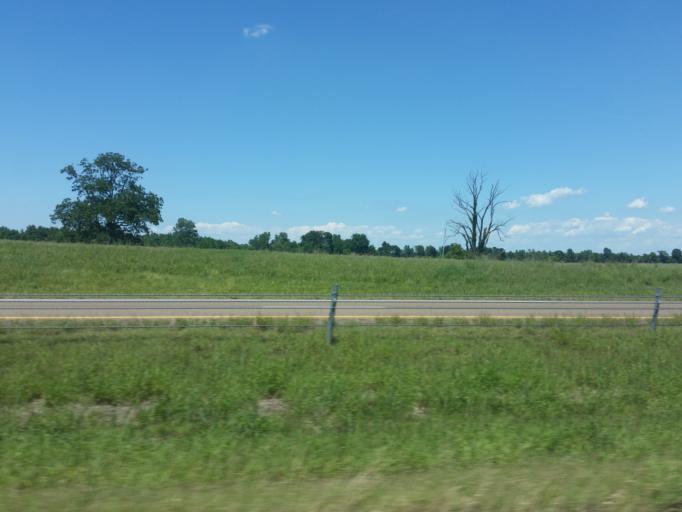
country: US
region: Missouri
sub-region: Pemiscot County
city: Caruthersville
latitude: 36.0925
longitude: -89.5833
